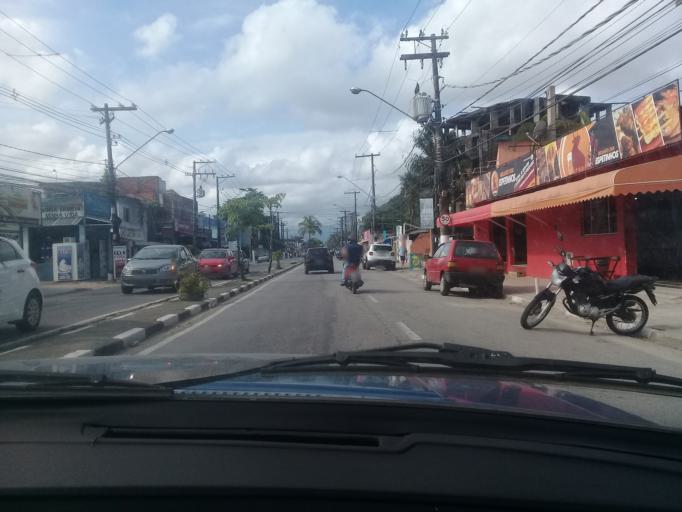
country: BR
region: Sao Paulo
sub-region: Guaruja
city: Guaruja
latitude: -24.0035
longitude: -46.2737
